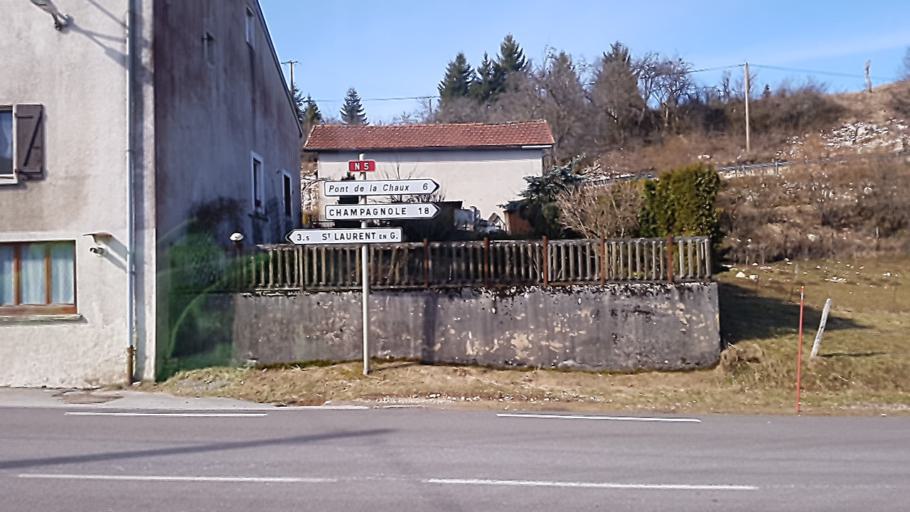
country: FR
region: Franche-Comte
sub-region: Departement du Jura
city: Morbier
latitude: 46.6078
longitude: 5.9623
